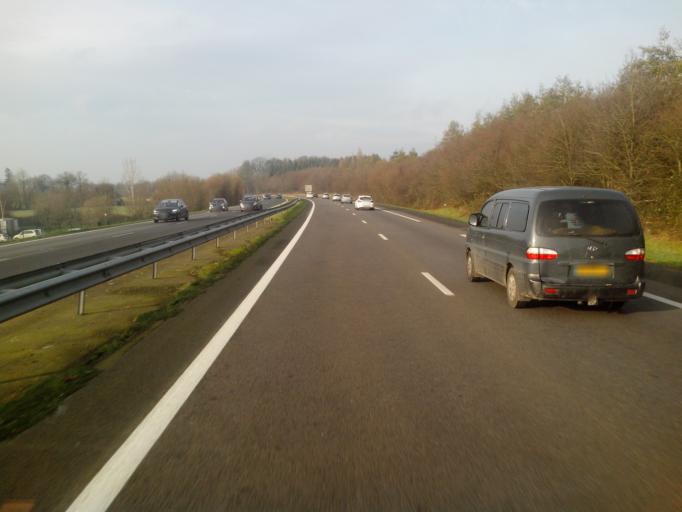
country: FR
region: Brittany
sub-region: Departement d'Ille-et-Vilaine
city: Montauban-de-Bretagne
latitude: 48.2005
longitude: -2.0301
